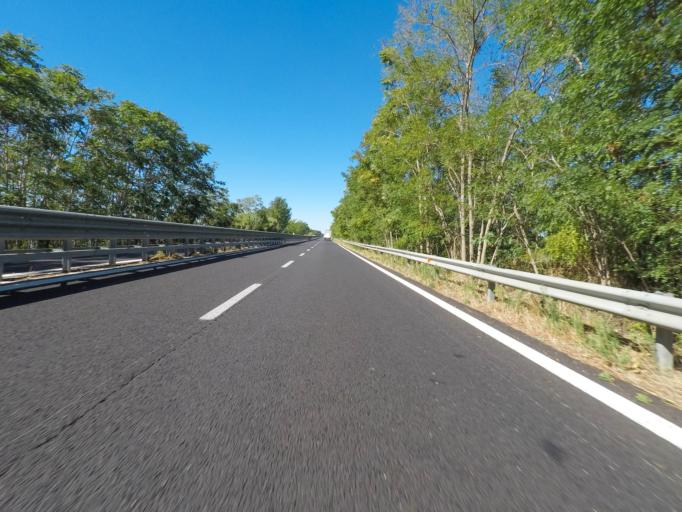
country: IT
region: Latium
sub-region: Provincia di Viterbo
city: Tarquinia
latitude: 42.2858
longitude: 11.6890
